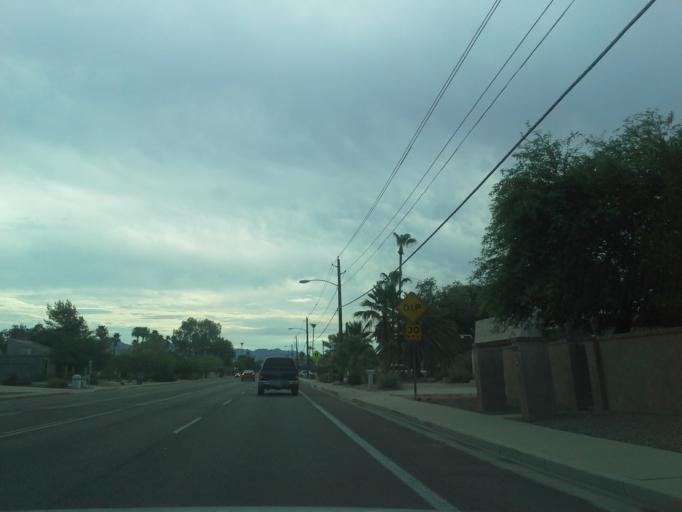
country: US
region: Arizona
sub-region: Maricopa County
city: Paradise Valley
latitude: 33.6113
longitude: -111.9366
